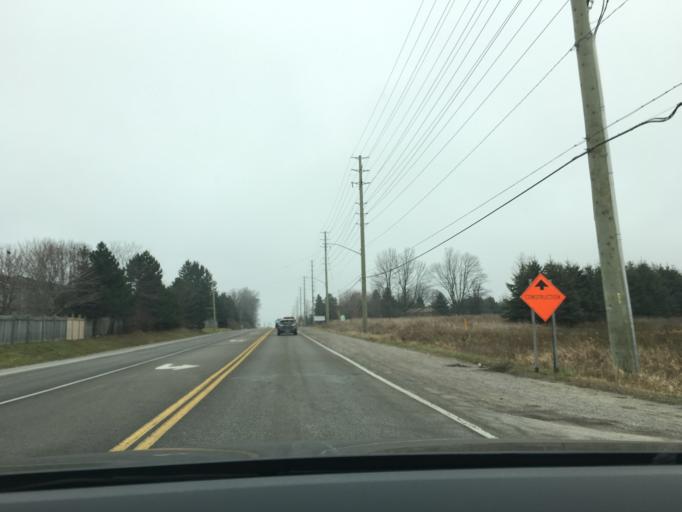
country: CA
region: Ontario
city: Innisfil
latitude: 44.3330
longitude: -79.7124
